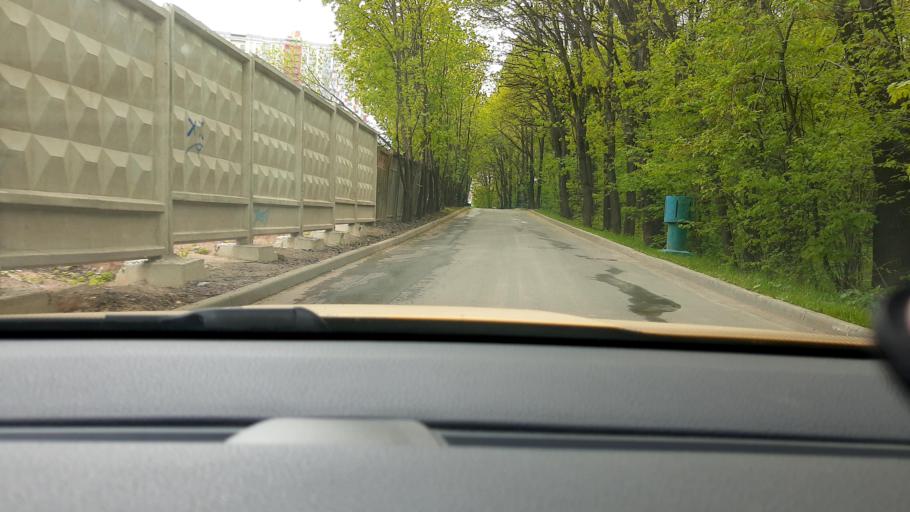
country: RU
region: Moskovskaya
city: Pavshino
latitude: 55.8487
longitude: 37.3756
